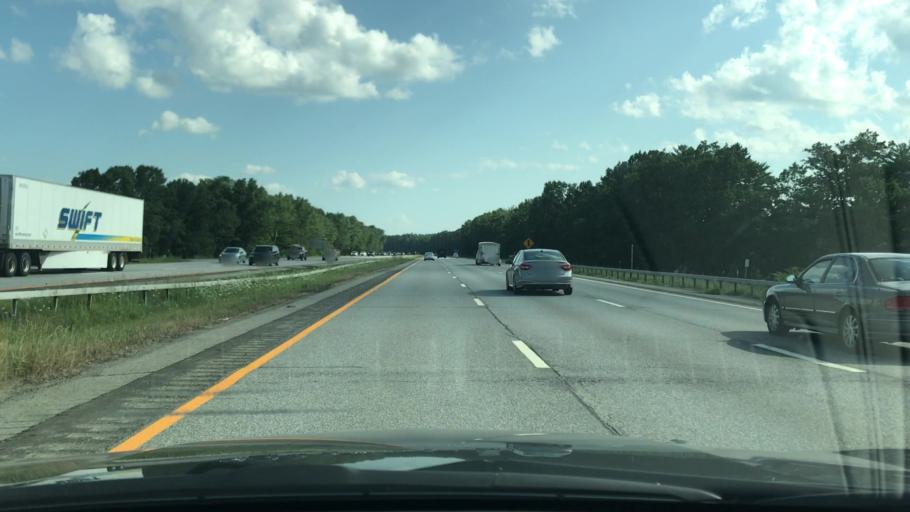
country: US
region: New York
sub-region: Warren County
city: West Glens Falls
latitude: 43.2972
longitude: -73.6793
